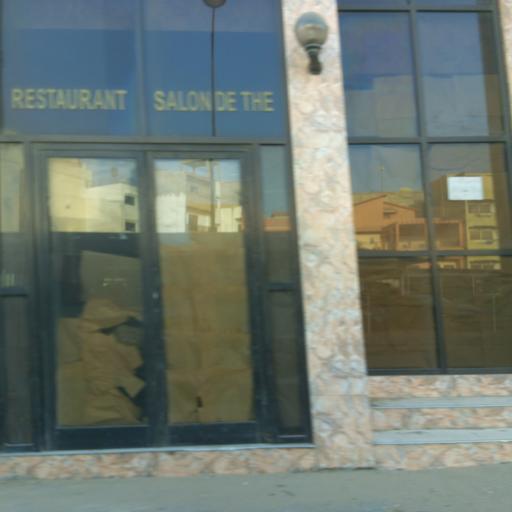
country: SN
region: Dakar
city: Grand Dakar
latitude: 14.7167
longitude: -17.4663
